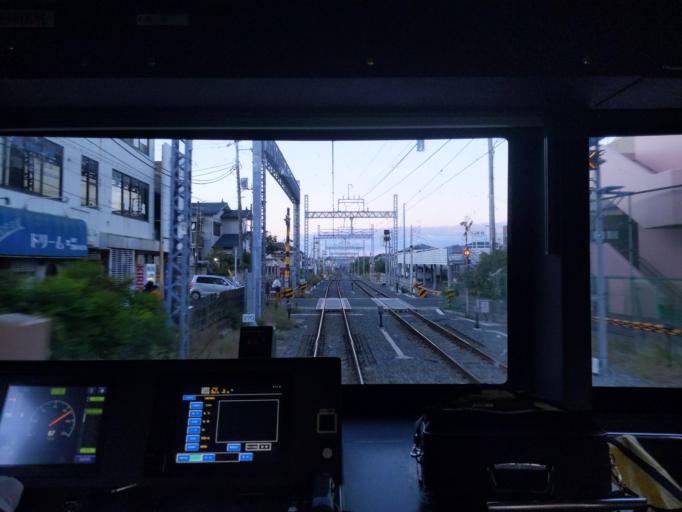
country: JP
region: Chiba
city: Kashiwa
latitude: 35.7946
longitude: 139.9992
